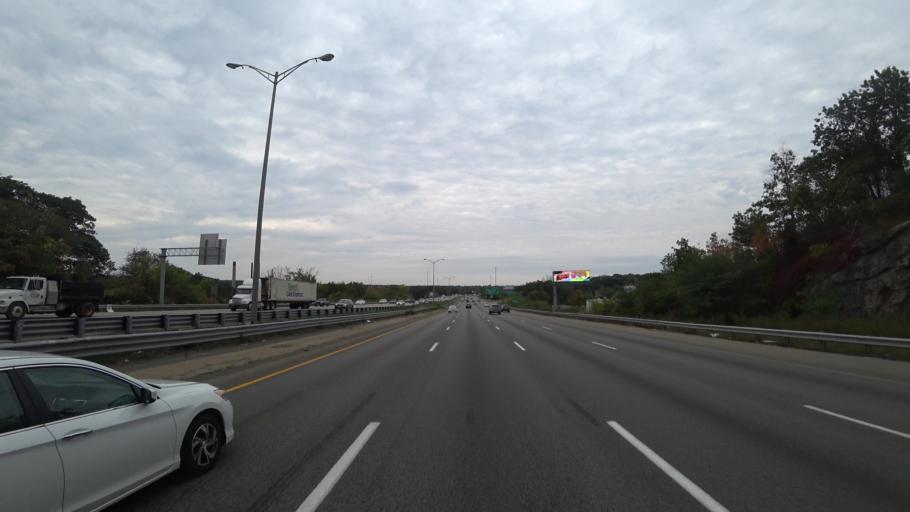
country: US
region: Massachusetts
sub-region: Middlesex County
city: Stoneham
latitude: 42.4765
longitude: -71.1123
